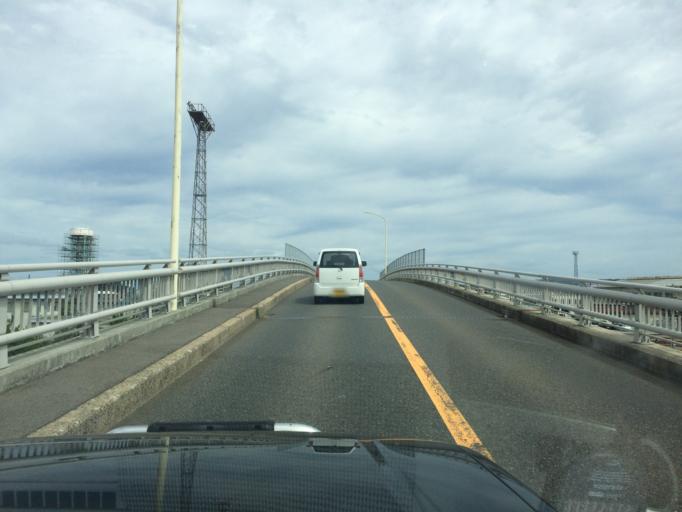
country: JP
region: Tottori
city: Tottori
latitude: 35.5091
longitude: 134.1940
